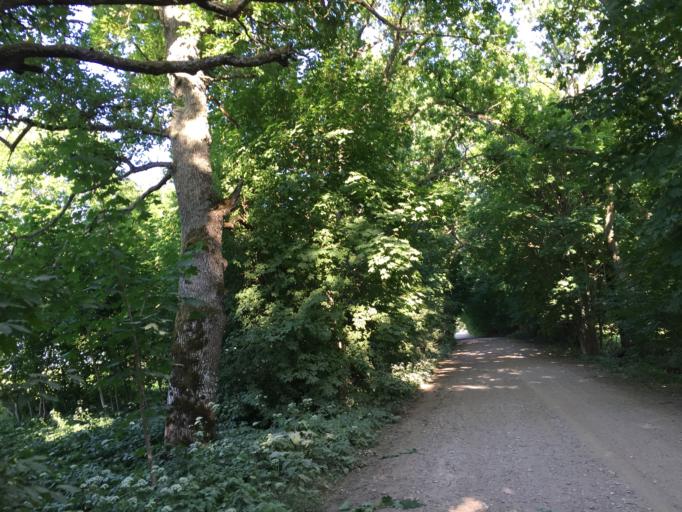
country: LV
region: Aizkraukles Rajons
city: Aizkraukle
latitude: 56.7895
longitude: 25.2716
